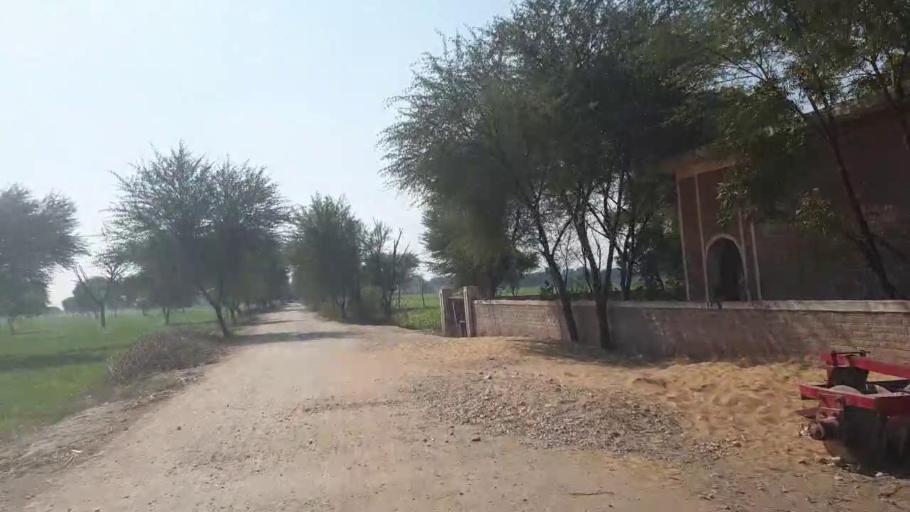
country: PK
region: Sindh
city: Tando Jam
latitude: 25.3016
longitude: 68.6343
